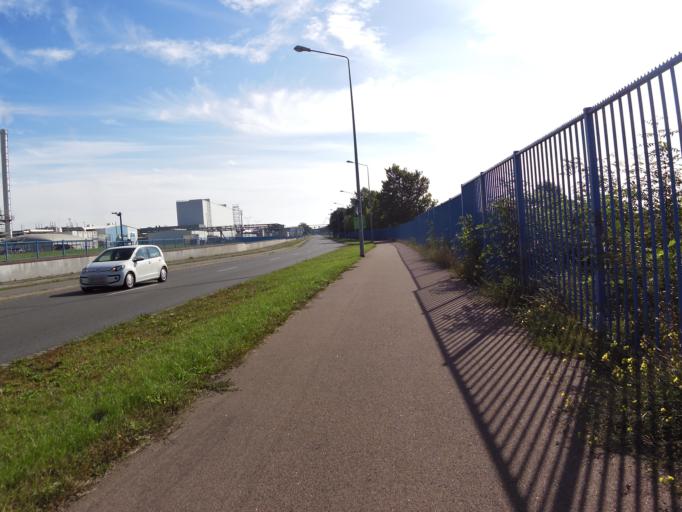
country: DE
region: Saxony-Anhalt
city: Wittenburg
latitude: 51.8701
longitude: 12.5752
